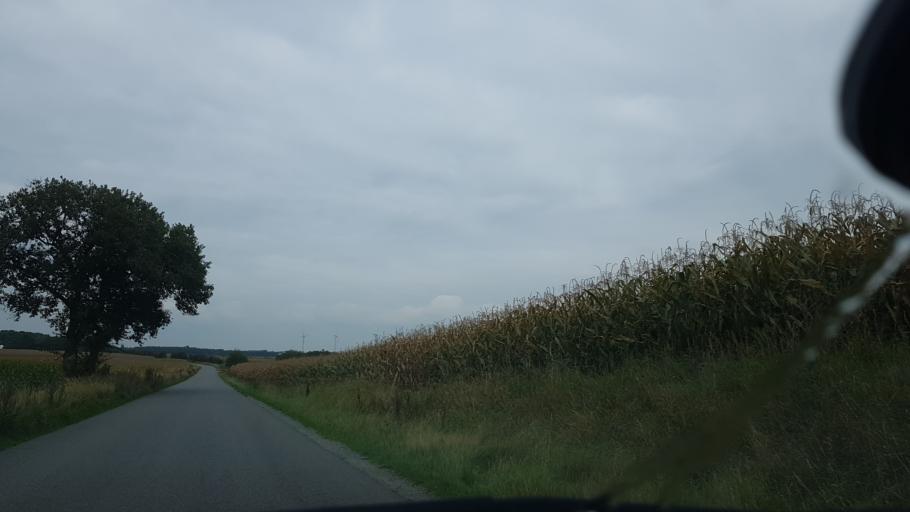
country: DK
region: South Denmark
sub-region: Vejle Kommune
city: Egtved
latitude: 55.5687
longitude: 9.2401
